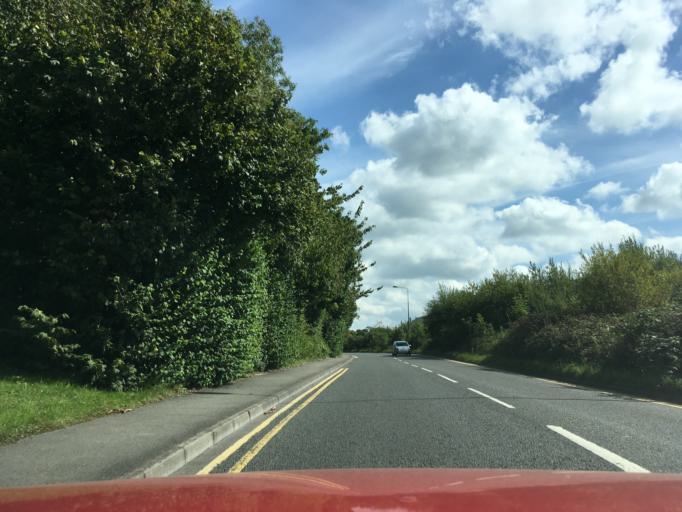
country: GB
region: England
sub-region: South Gloucestershire
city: Thornbury
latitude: 51.6039
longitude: -2.5217
